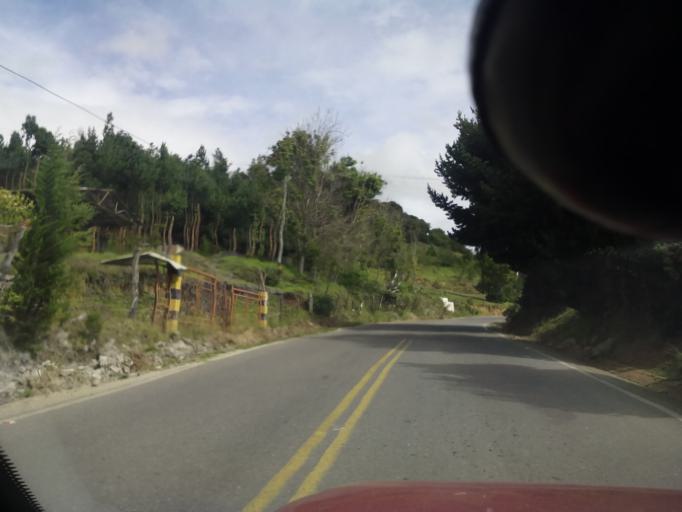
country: CO
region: Boyaca
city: Combita
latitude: 5.6302
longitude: -73.3169
